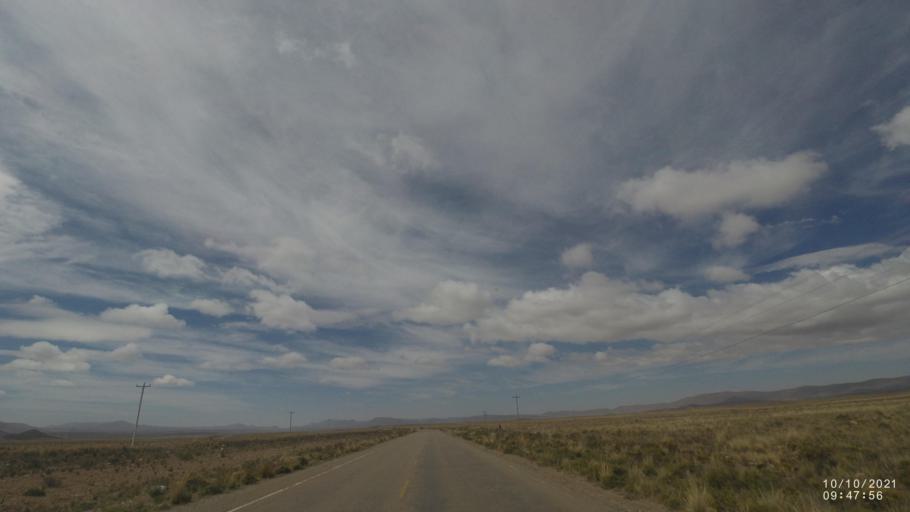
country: BO
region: La Paz
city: Quime
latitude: -17.2014
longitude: -67.3423
